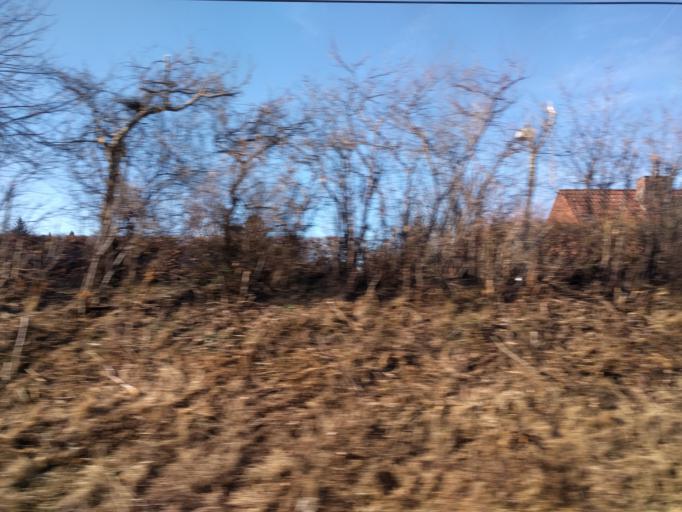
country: DK
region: Capital Region
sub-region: Horsholm Kommune
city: Horsholm
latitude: 55.8885
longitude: 12.5225
